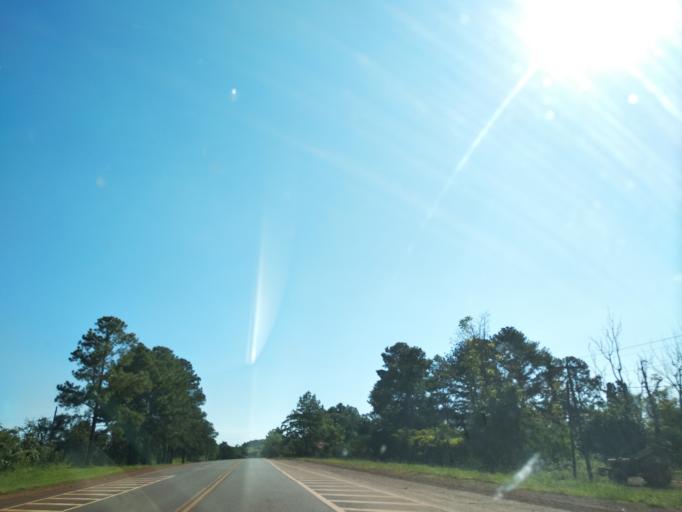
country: AR
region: Misiones
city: Garuhape
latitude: -26.8219
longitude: -54.9734
